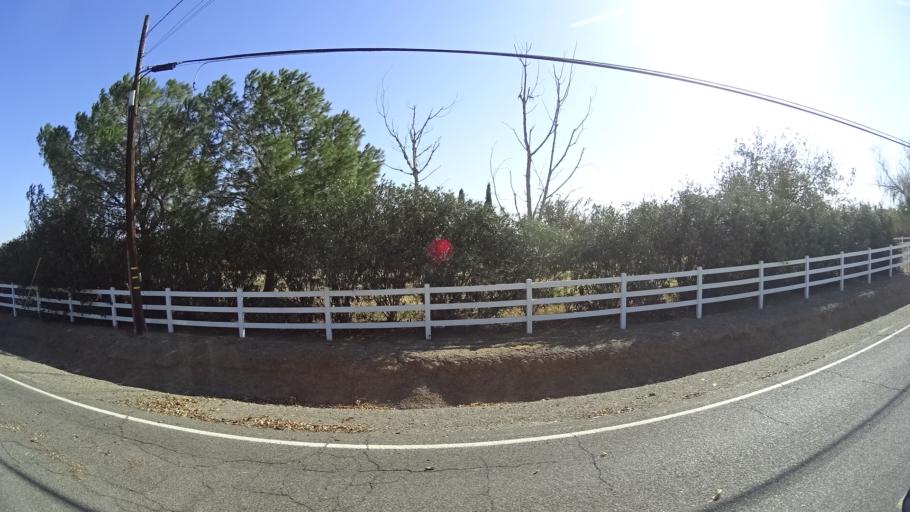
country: US
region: California
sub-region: Yolo County
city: Woodland
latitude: 38.6756
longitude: -121.8693
